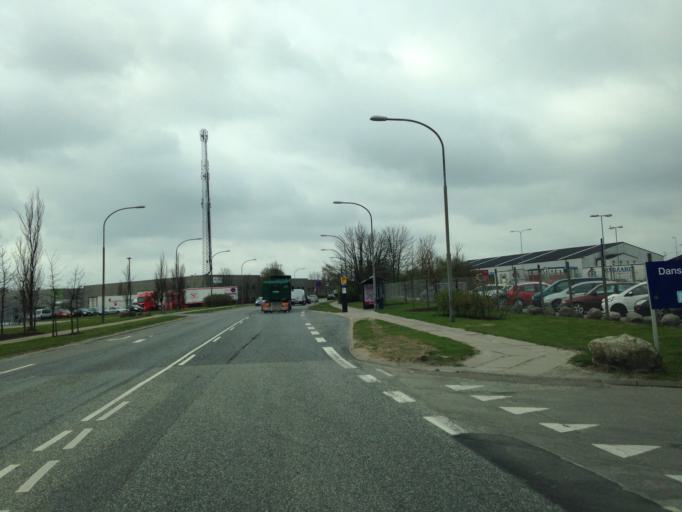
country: DK
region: Capital Region
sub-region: Ishoj Kommune
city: Ishoj
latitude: 55.6205
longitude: 12.3354
